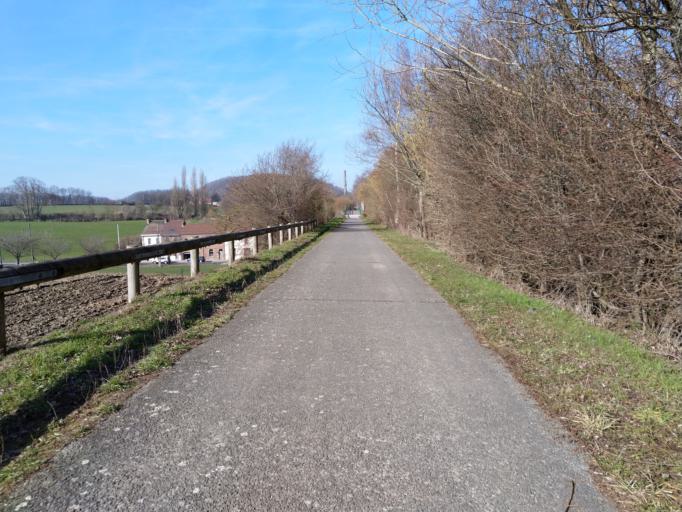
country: BE
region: Wallonia
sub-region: Province du Hainaut
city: Frameries
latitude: 50.4294
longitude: 3.9169
